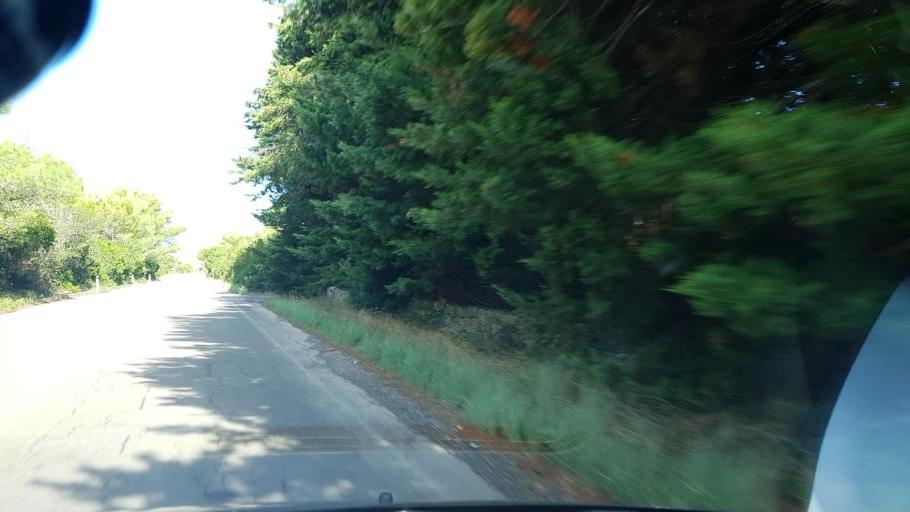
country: IT
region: Apulia
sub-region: Provincia di Lecce
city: Borgagne
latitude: 40.2472
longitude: 18.4414
